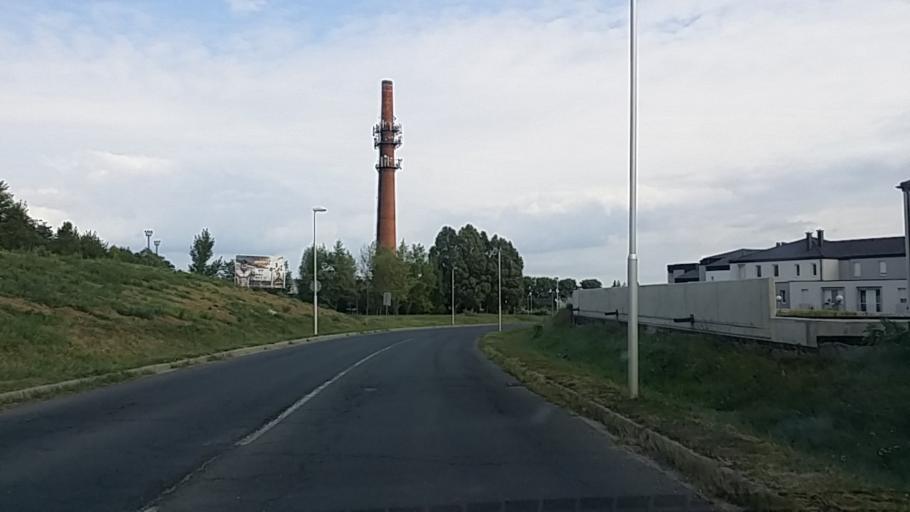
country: HU
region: Gyor-Moson-Sopron
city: Sopron
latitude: 47.6864
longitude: 16.6073
